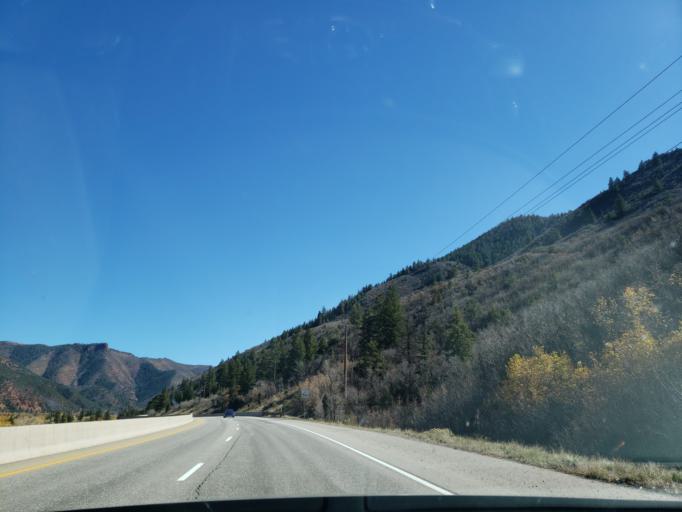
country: US
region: Colorado
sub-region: Eagle County
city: Basalt
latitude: 39.3298
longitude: -106.9777
